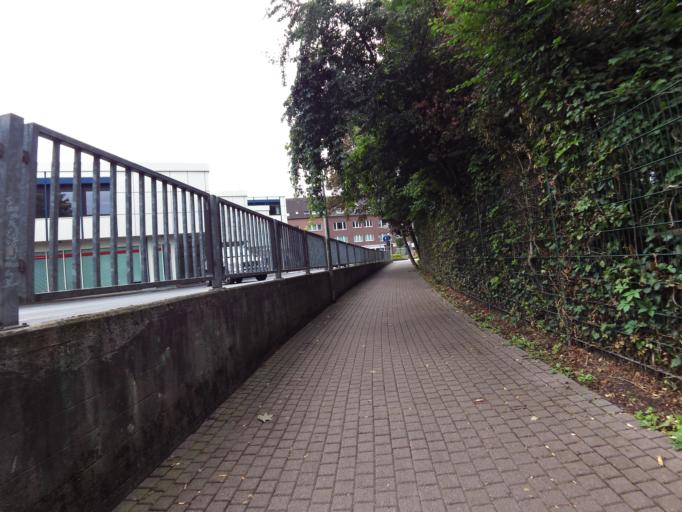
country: DE
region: North Rhine-Westphalia
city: Geilenkirchen
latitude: 50.9635
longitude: 6.1233
